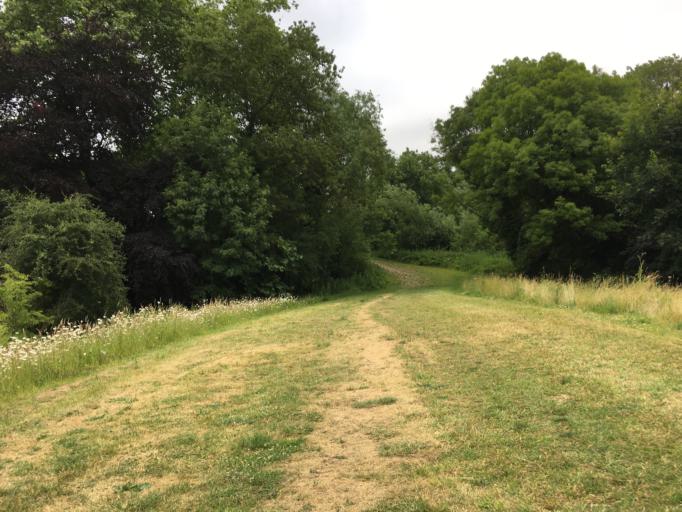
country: GB
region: England
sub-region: Greater London
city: Belsize Park
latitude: 51.5619
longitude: -0.1678
